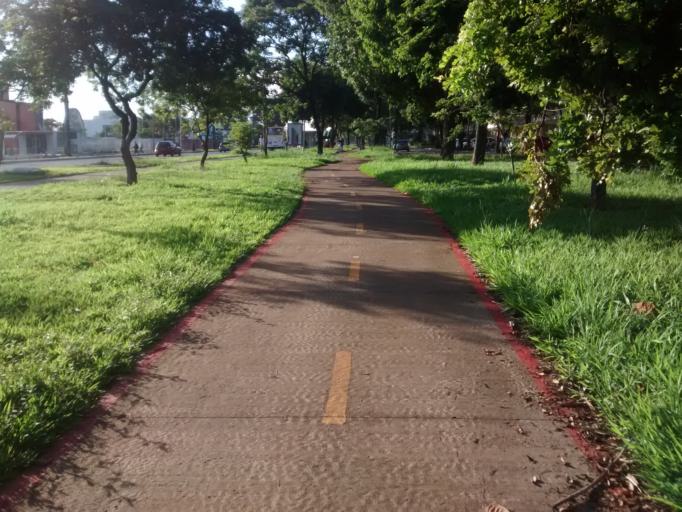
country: BR
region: Federal District
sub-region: Brasilia
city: Brasilia
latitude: -15.7569
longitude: -47.8792
